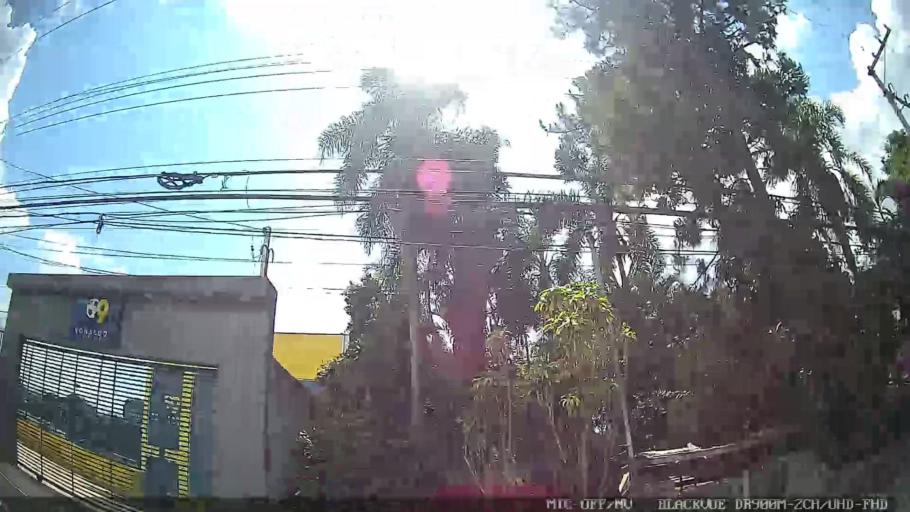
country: BR
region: Sao Paulo
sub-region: Ferraz De Vasconcelos
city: Ferraz de Vasconcelos
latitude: -23.5481
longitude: -46.4617
